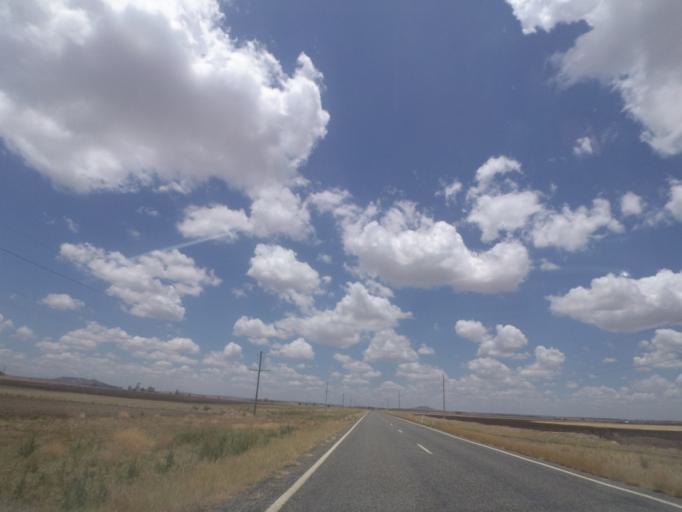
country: AU
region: Queensland
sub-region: Toowoomba
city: Top Camp
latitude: -27.8984
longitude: 151.9755
